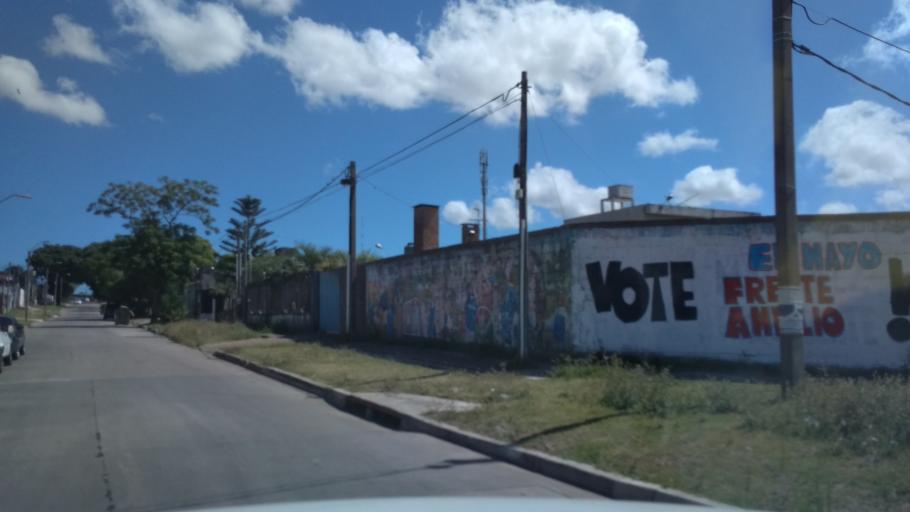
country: UY
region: Canelones
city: La Paz
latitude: -34.8264
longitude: -56.2225
